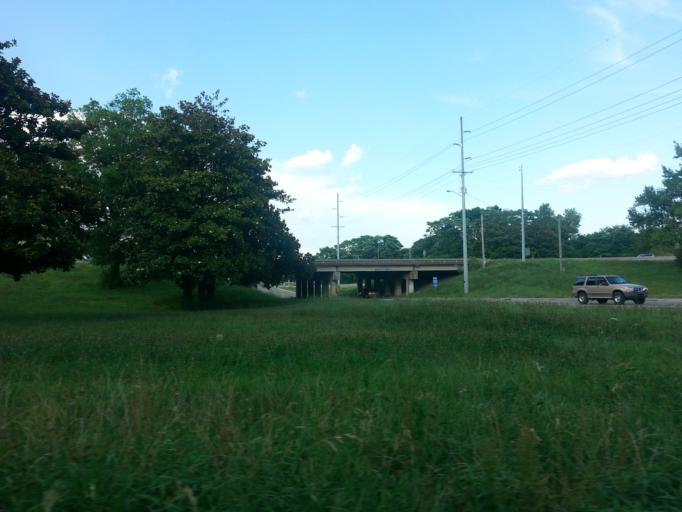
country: US
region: Tennessee
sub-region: Knox County
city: Knoxville
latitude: 35.9811
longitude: -83.9391
